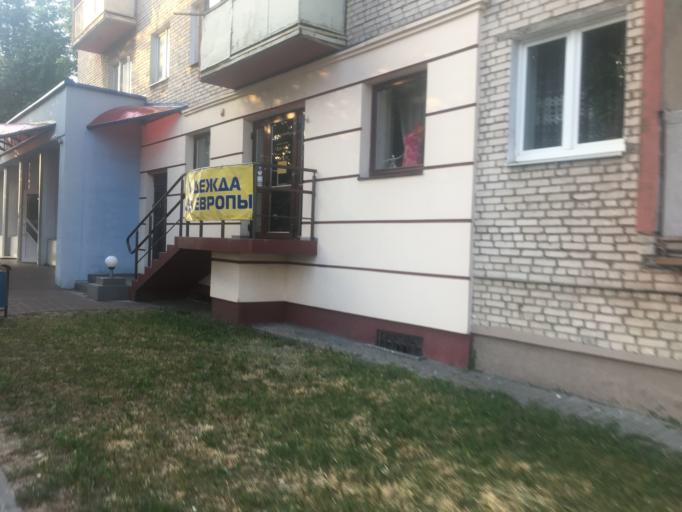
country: BY
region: Grodnenskaya
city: Hrodna
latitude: 53.6965
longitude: 23.8213
